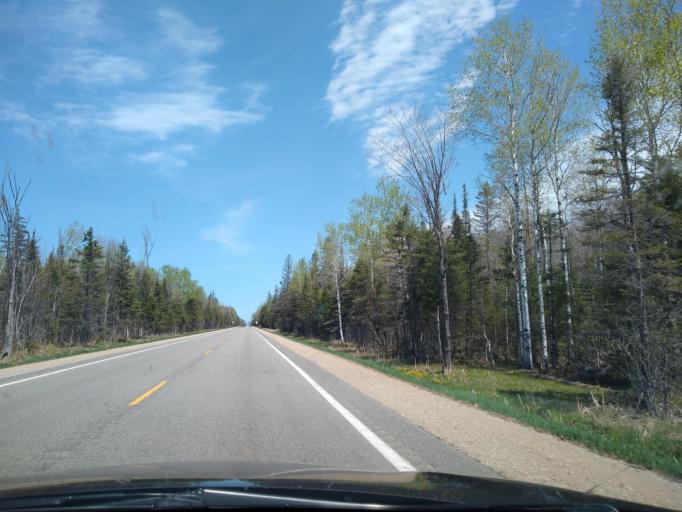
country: US
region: Michigan
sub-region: Delta County
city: Gladstone
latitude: 46.0469
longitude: -86.9814
